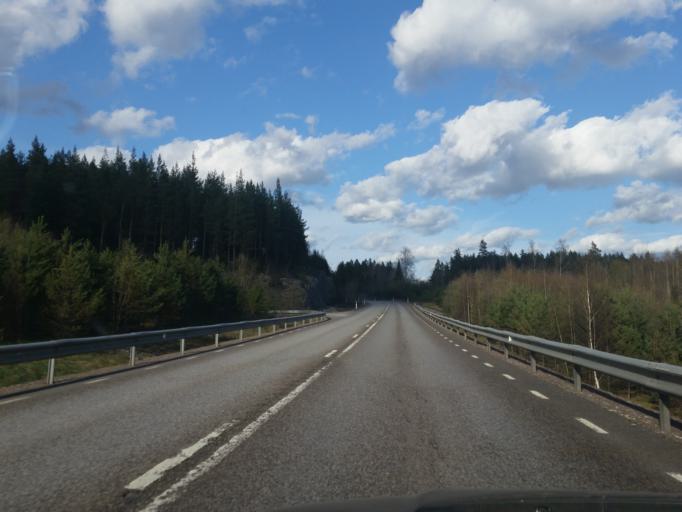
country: SE
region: Kalmar
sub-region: Hultsfreds Kommun
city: Virserum
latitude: 57.3533
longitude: 15.6328
